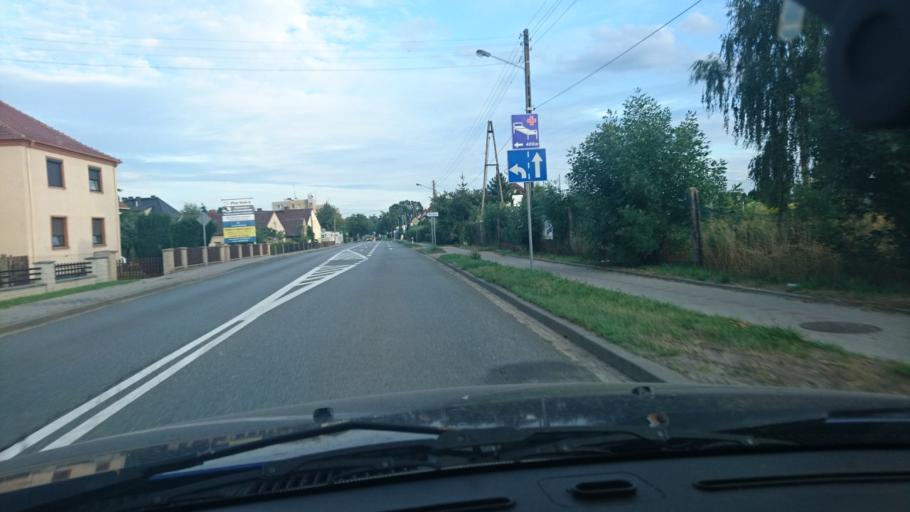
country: PL
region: Opole Voivodeship
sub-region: Powiat oleski
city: Olesno
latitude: 50.8795
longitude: 18.4104
